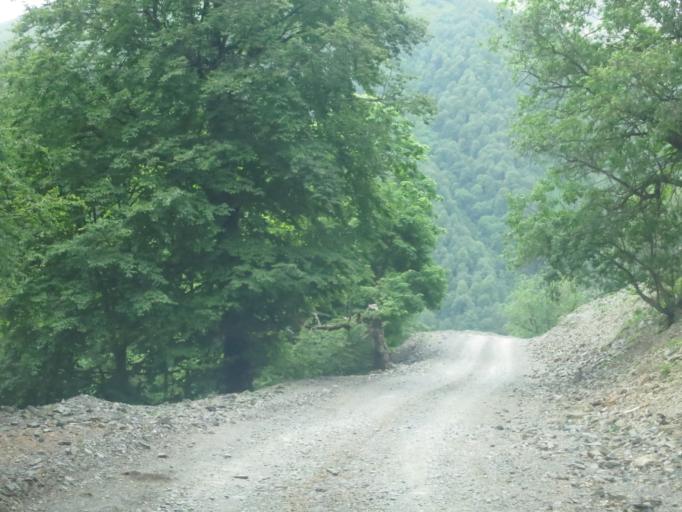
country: GE
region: Kakheti
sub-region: Telavi
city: Telavi
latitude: 42.2493
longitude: 45.4994
